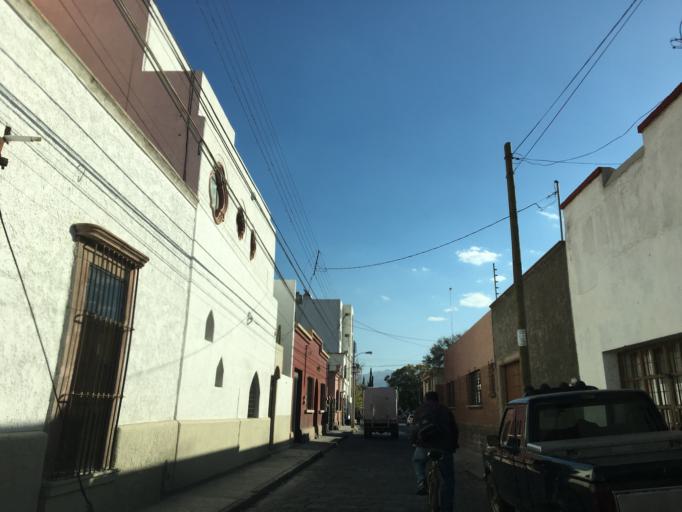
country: MX
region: San Luis Potosi
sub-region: San Luis Potosi
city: San Luis Potosi
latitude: 22.1483
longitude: -100.9927
